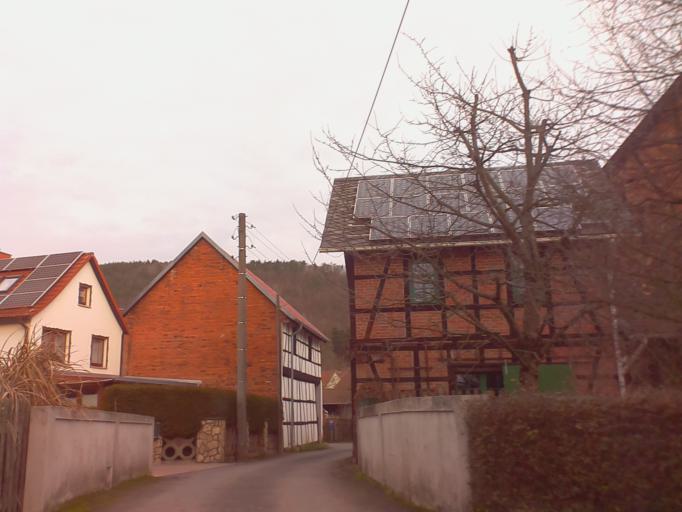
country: DE
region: Thuringia
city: Grosseutersdorf
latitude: 50.7888
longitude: 11.5665
